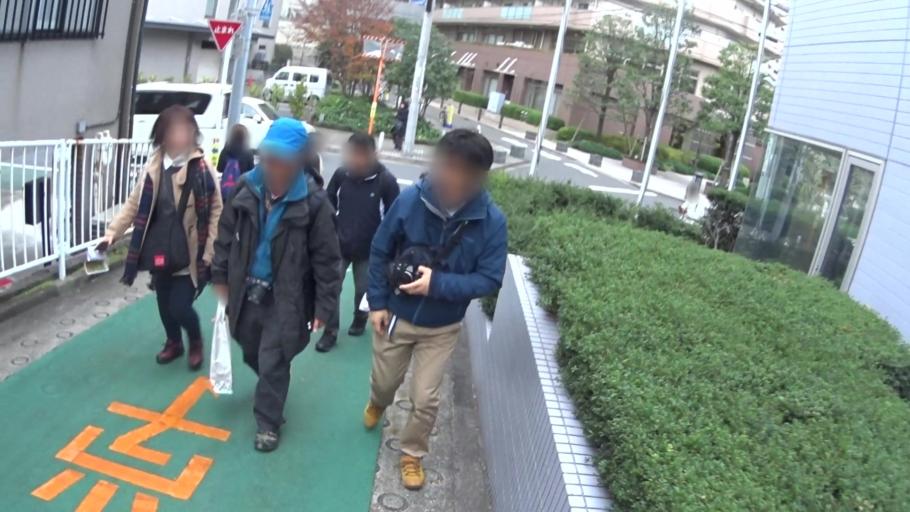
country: JP
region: Tokyo
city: Tokyo
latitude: 35.6924
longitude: 139.7156
